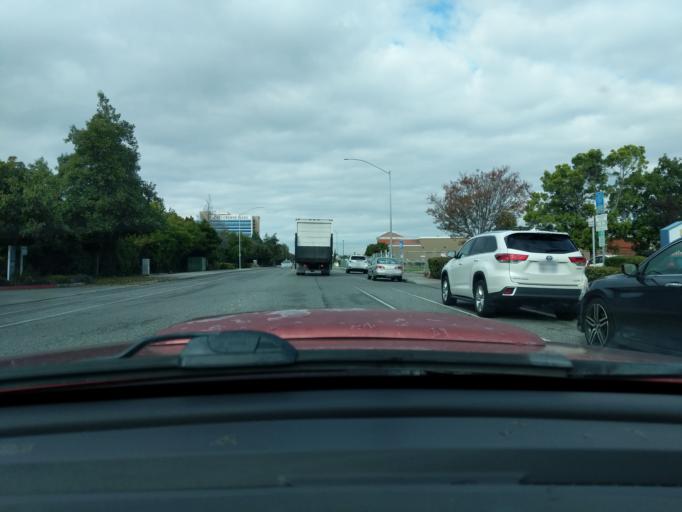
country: US
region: California
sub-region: Santa Clara County
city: Milpitas
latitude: 37.4194
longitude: -121.9165
